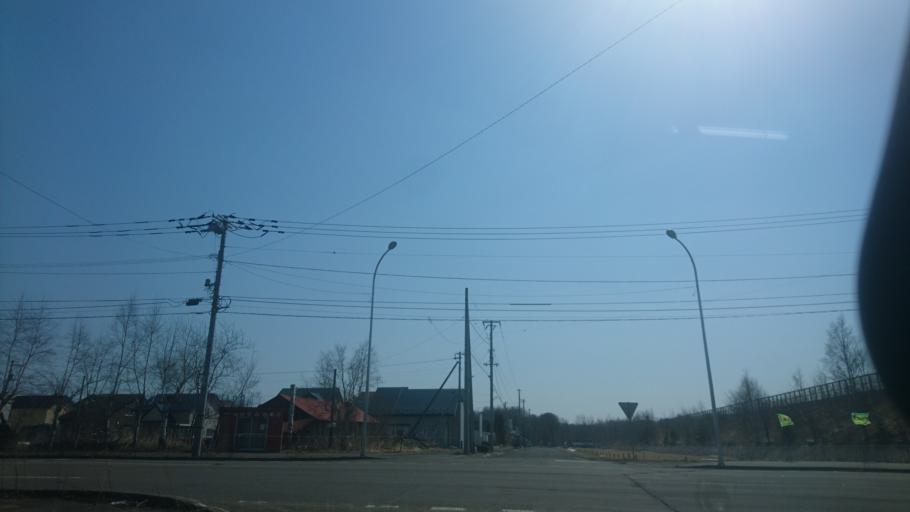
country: JP
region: Hokkaido
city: Obihiro
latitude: 42.9156
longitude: 143.1107
